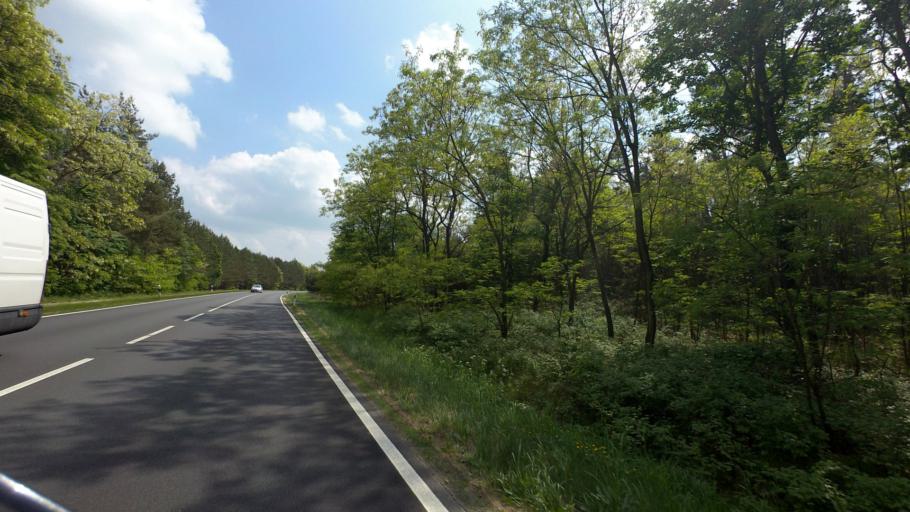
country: DE
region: Saxony
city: Niesky
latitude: 51.3217
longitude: 14.8246
